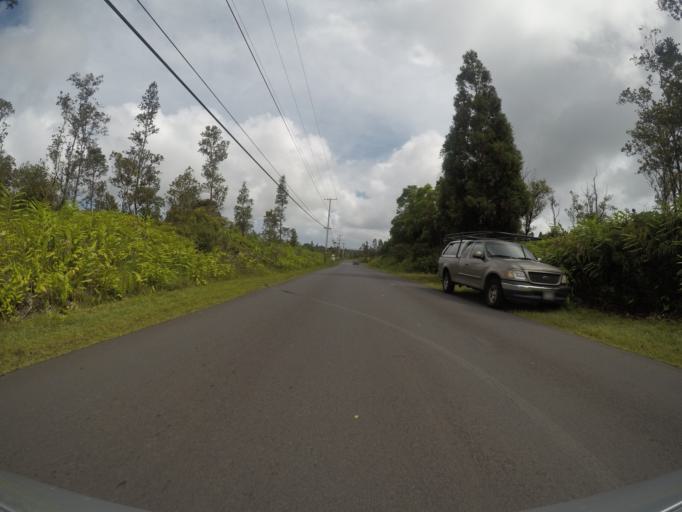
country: US
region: Hawaii
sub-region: Hawaii County
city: Fern Acres
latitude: 19.4771
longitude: -155.1413
